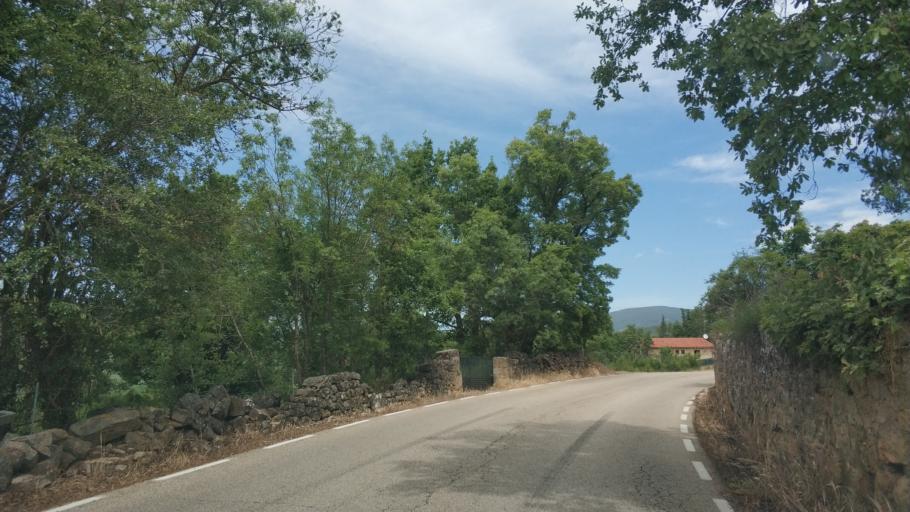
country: ES
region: Castille and Leon
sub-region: Provincia de Soria
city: Sotillo del Rincon
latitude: 41.8958
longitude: -2.6378
